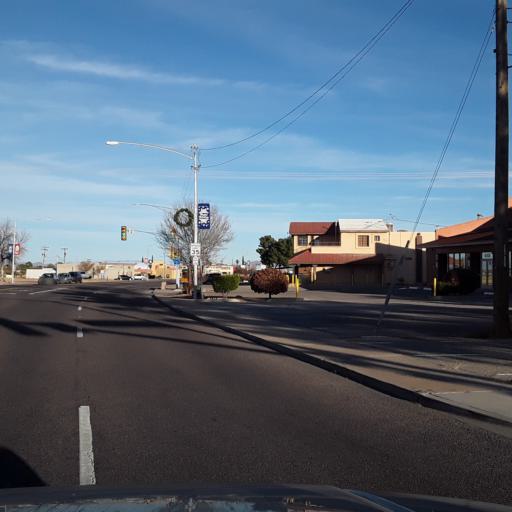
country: US
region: Arizona
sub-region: Cochise County
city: Sierra Vista
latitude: 31.5539
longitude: -110.3064
